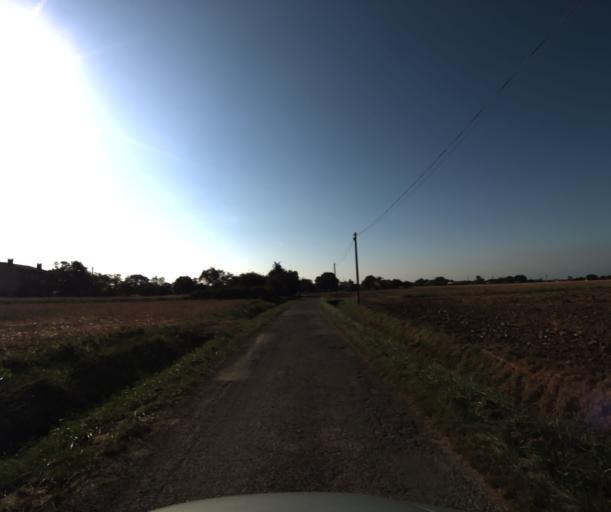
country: FR
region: Midi-Pyrenees
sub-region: Departement de la Haute-Garonne
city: Labarthe-sur-Leze
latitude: 43.4514
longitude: 1.3797
